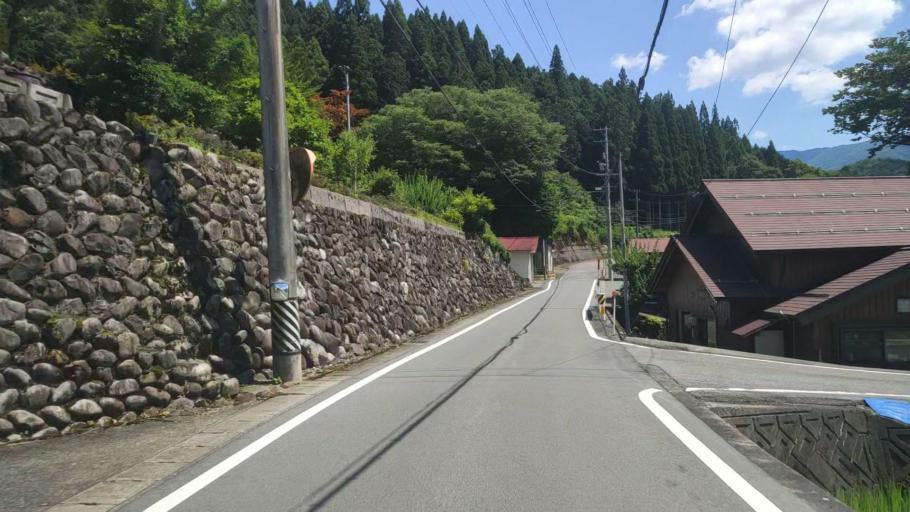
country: JP
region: Gifu
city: Godo
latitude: 35.6696
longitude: 136.5778
